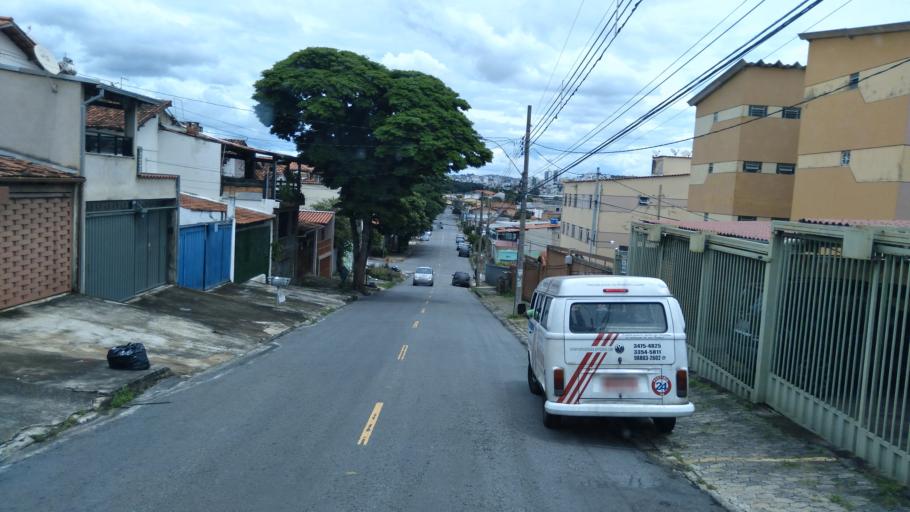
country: BR
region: Minas Gerais
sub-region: Belo Horizonte
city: Belo Horizonte
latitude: -19.8532
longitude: -43.9179
